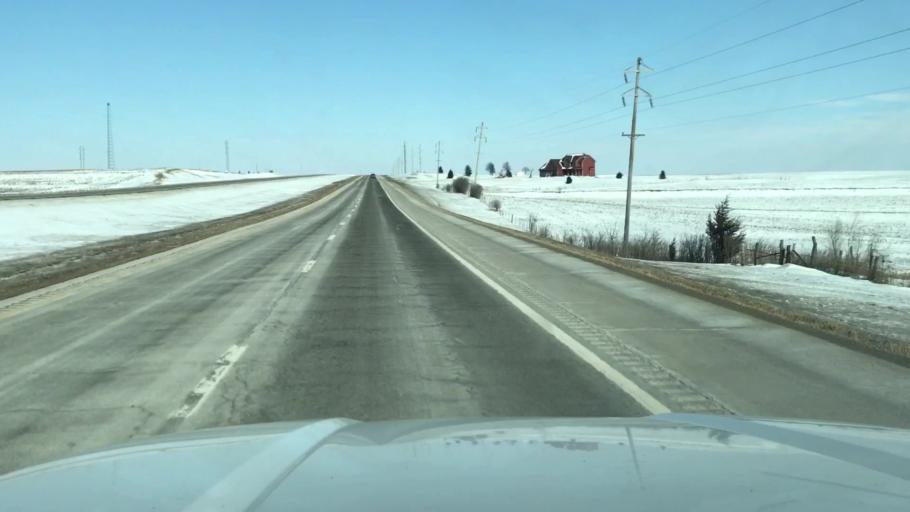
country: US
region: Missouri
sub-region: Nodaway County
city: Maryville
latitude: 40.2219
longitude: -94.8678
